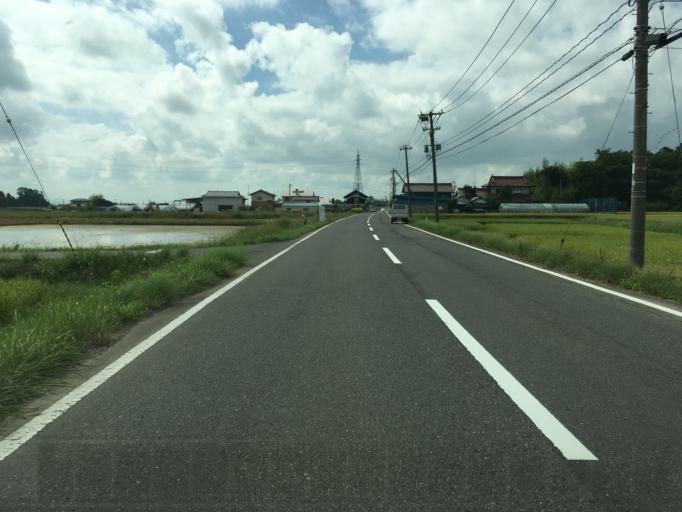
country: JP
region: Fukushima
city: Motomiya
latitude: 37.4688
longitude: 140.3406
